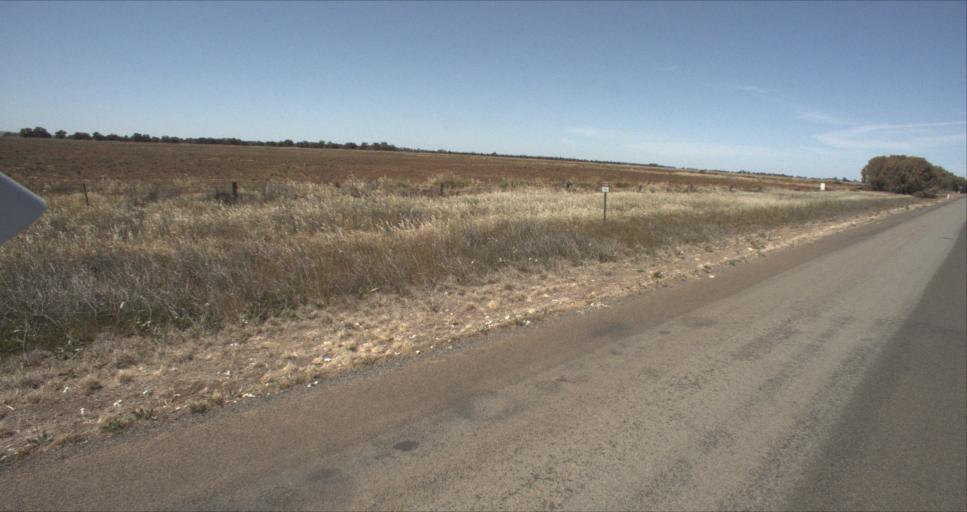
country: AU
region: New South Wales
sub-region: Leeton
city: Leeton
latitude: -34.4801
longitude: 146.2907
